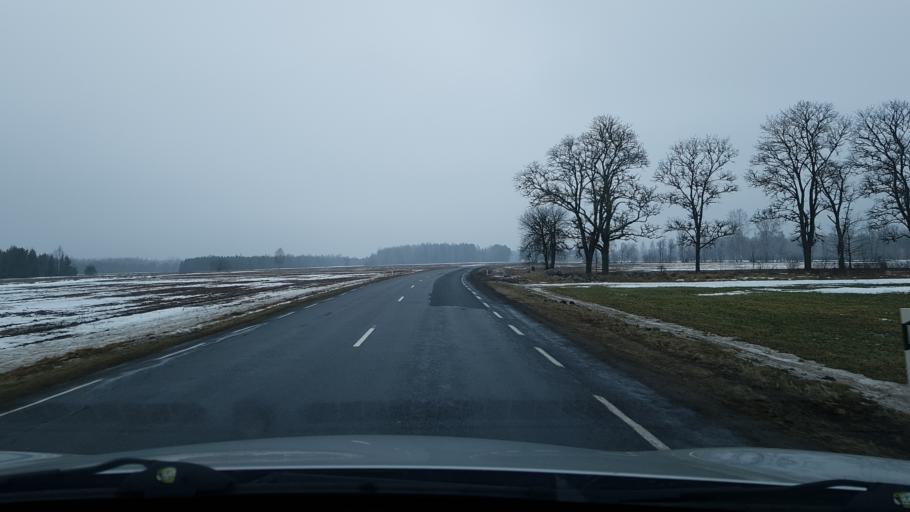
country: EE
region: Valgamaa
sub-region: Torva linn
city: Torva
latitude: 58.1904
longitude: 25.9512
